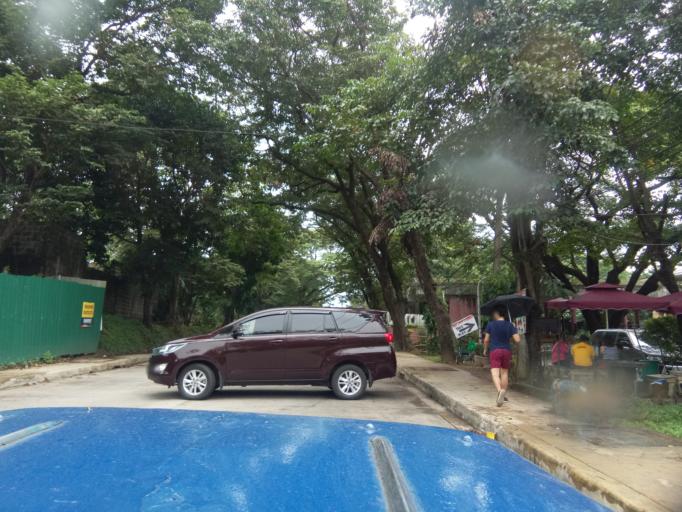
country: PH
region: Metro Manila
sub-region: Quezon City
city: Quezon City
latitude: 14.6576
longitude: 121.0633
